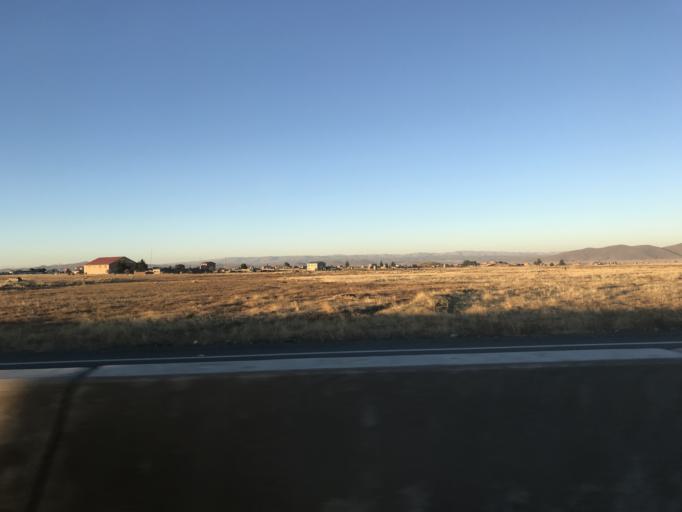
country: BO
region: La Paz
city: Batallas
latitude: -16.3087
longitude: -68.4655
